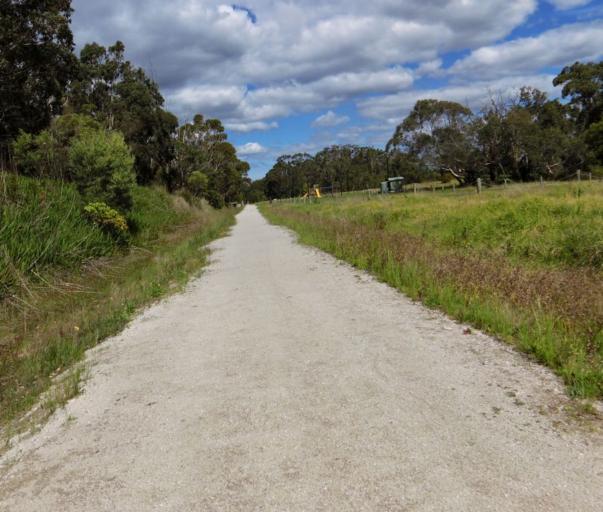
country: AU
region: Victoria
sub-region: Bass Coast
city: North Wonthaggi
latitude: -38.6524
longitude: 146.0285
